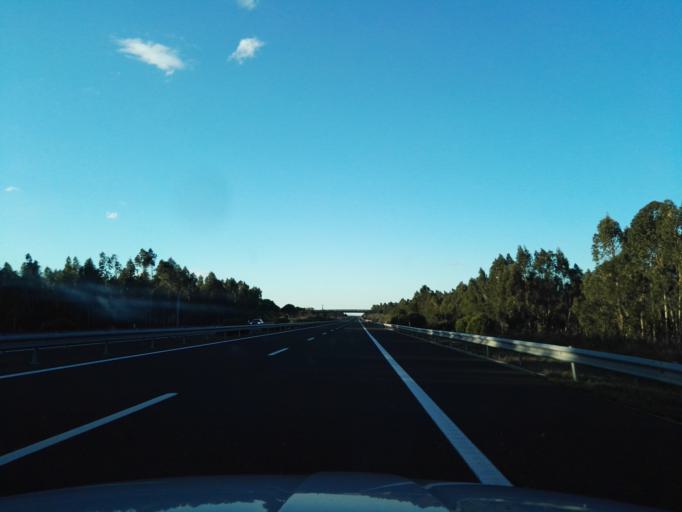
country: PT
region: Santarem
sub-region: Benavente
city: Poceirao
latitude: 38.7938
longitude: -8.6921
